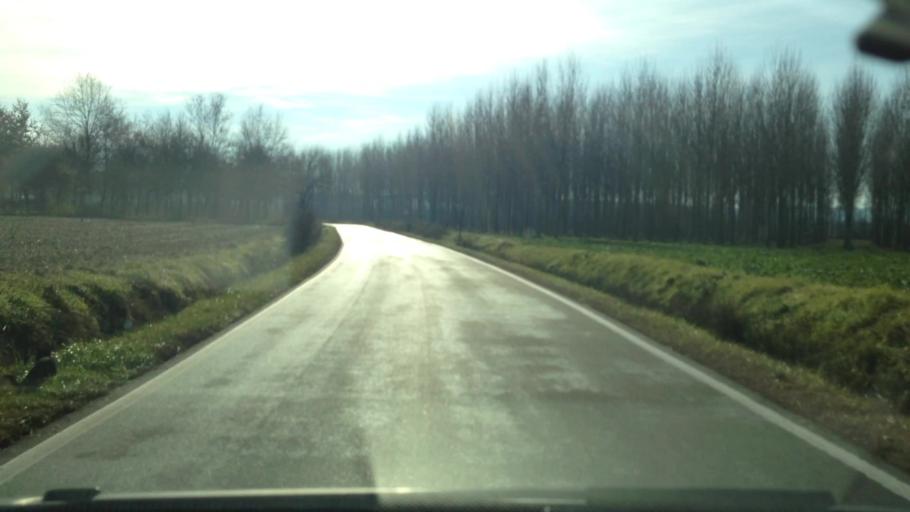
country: IT
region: Piedmont
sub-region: Provincia di Alessandria
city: Quattordio
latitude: 44.8878
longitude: 8.4045
